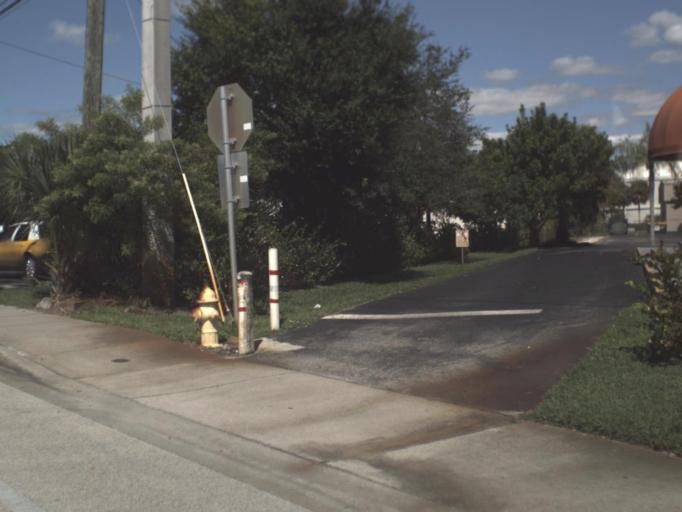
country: US
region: Florida
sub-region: Collier County
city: Naples
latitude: 26.1305
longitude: -81.7712
